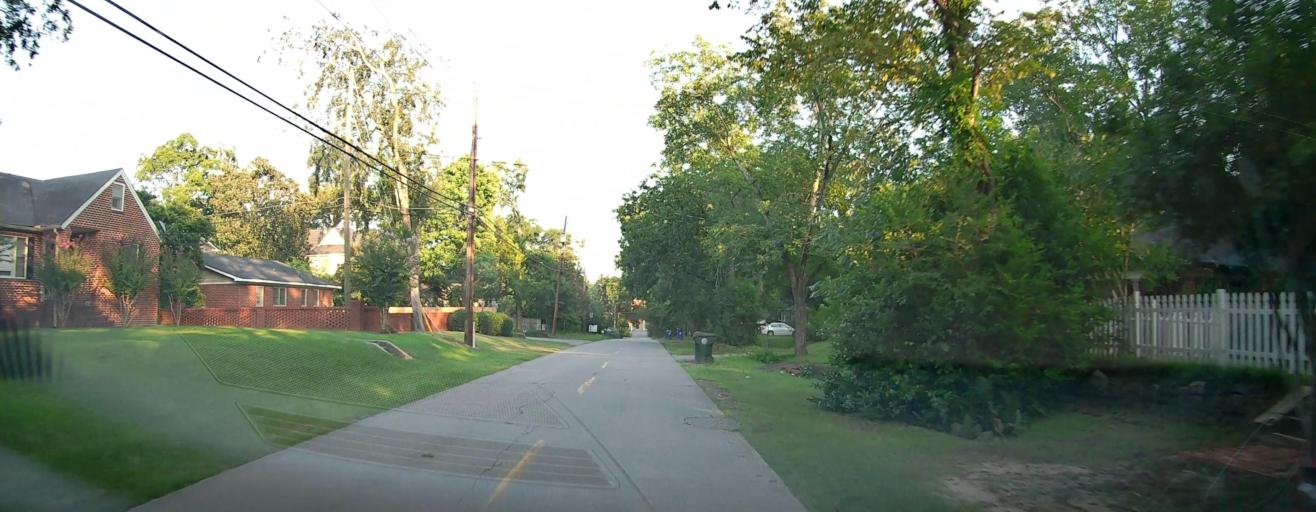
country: US
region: Georgia
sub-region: Bibb County
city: Macon
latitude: 32.8501
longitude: -83.6719
